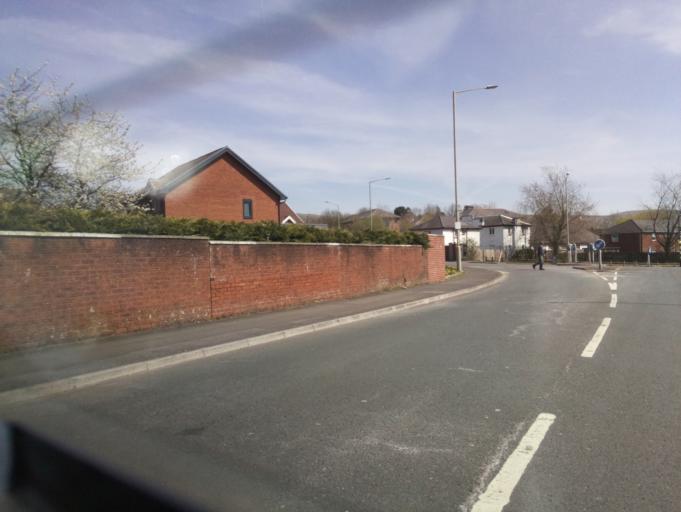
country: GB
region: Wales
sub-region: Merthyr Tydfil County Borough
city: Merthyr Tydfil
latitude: 51.7490
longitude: -3.3855
